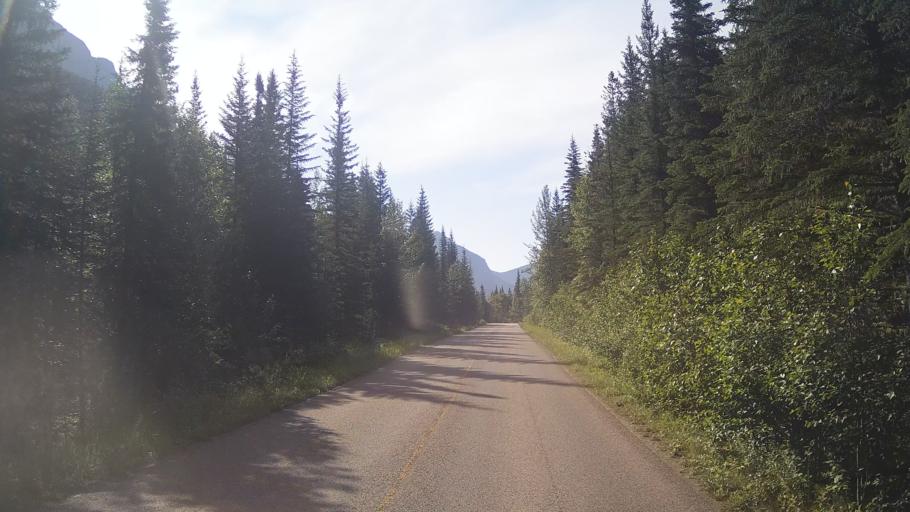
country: CA
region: Alberta
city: Hinton
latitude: 53.1754
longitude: -117.8301
